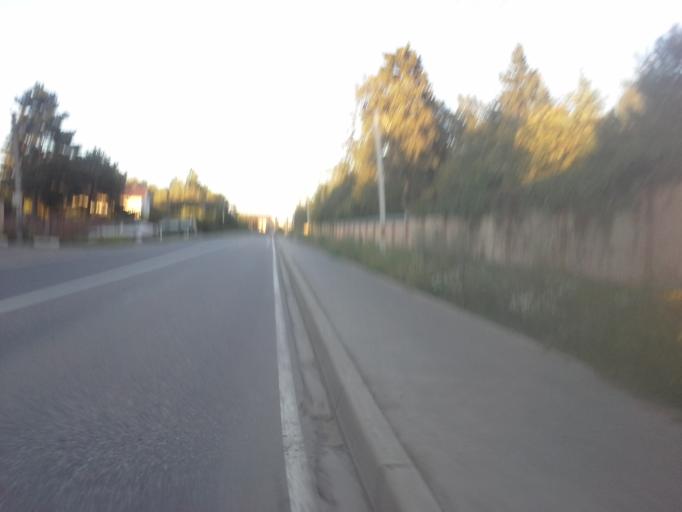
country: RU
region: Moskovskaya
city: Selyatino
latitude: 55.5175
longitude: 36.9473
